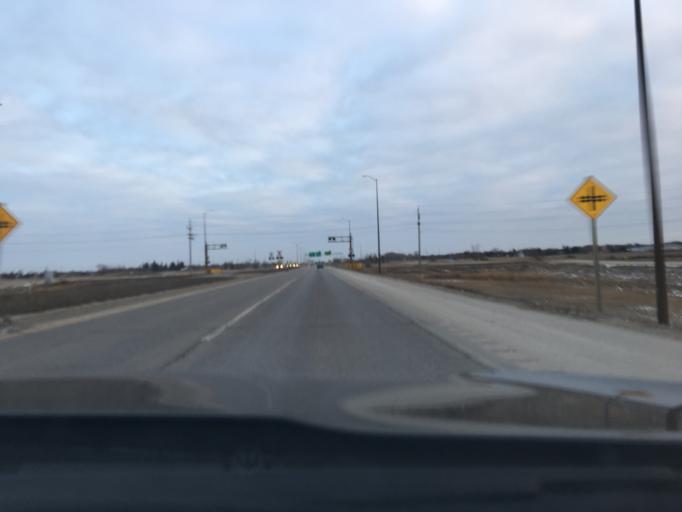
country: CA
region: Manitoba
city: Winnipeg
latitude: 49.9761
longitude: -97.0829
